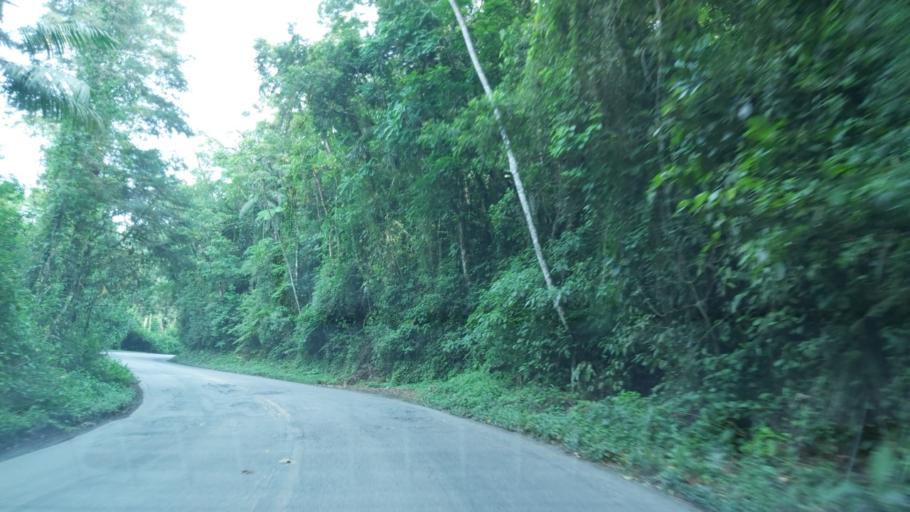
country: BR
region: Sao Paulo
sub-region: Miracatu
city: Miracatu
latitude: -24.0436
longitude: -47.5681
